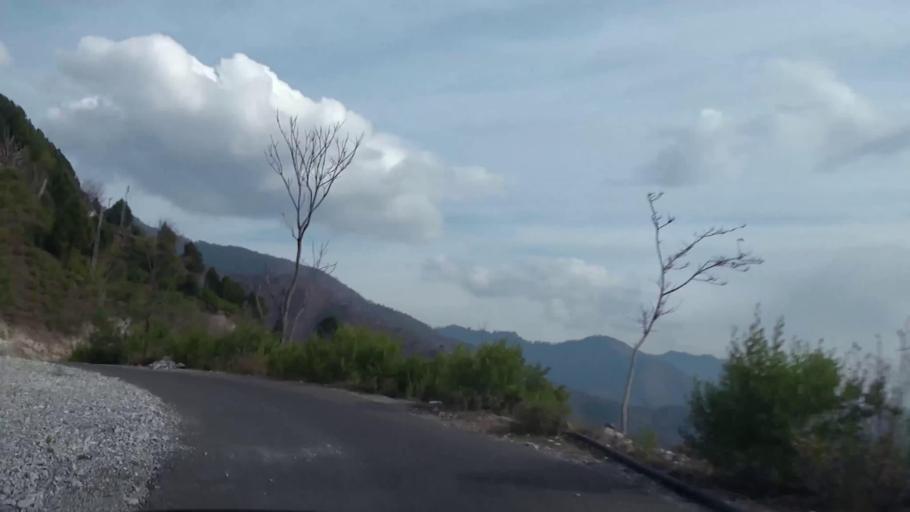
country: PK
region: Azad Kashmir
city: Muzaffarabad
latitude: 34.3616
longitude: 73.5071
